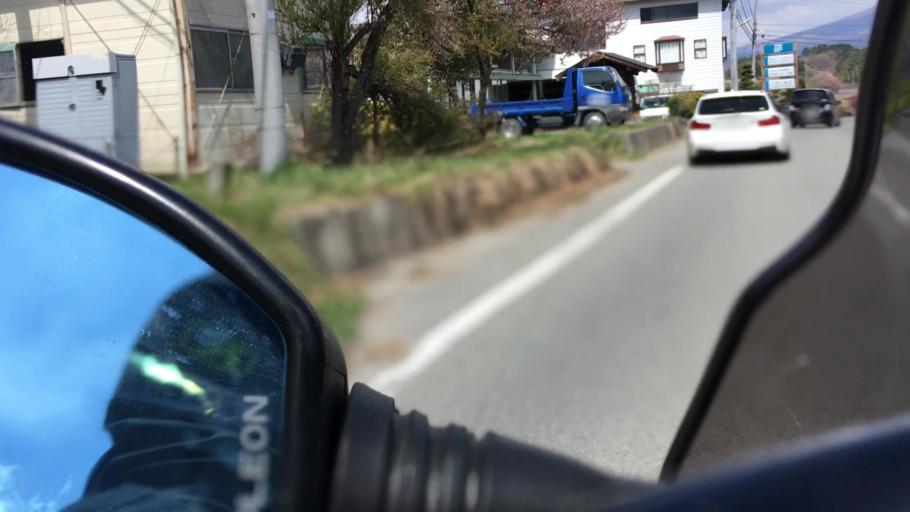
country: JP
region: Yamanashi
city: Nirasaki
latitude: 35.7868
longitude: 138.3213
